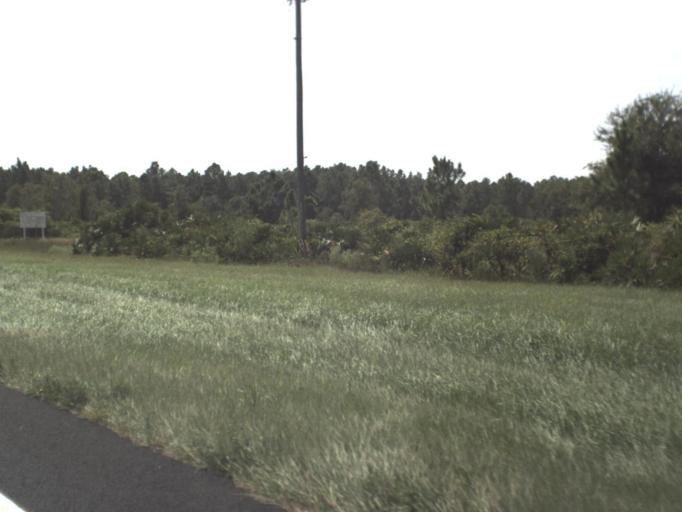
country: US
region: Florida
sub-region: Polk County
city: Frostproof
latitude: 27.7236
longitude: -81.5657
